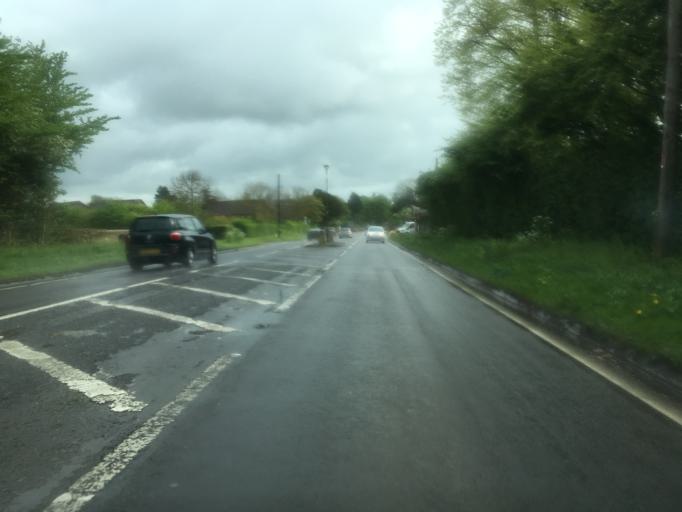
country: GB
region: England
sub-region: North Somerset
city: Burrington
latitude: 51.3405
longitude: -2.7620
